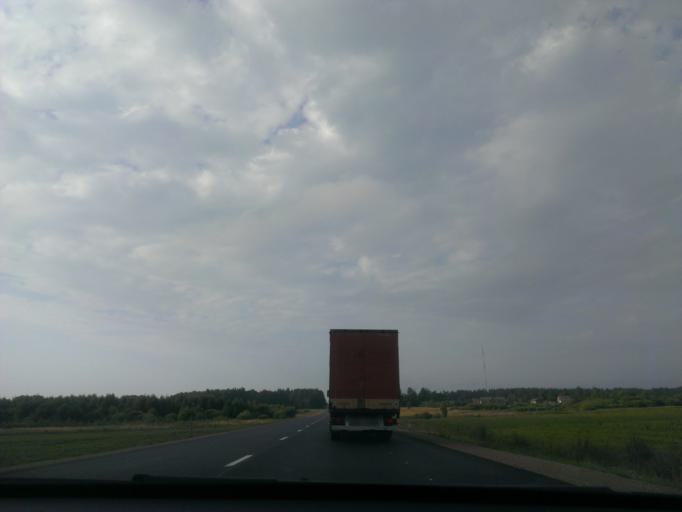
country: LV
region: Lecava
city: Iecava
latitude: 56.6561
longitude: 24.2311
